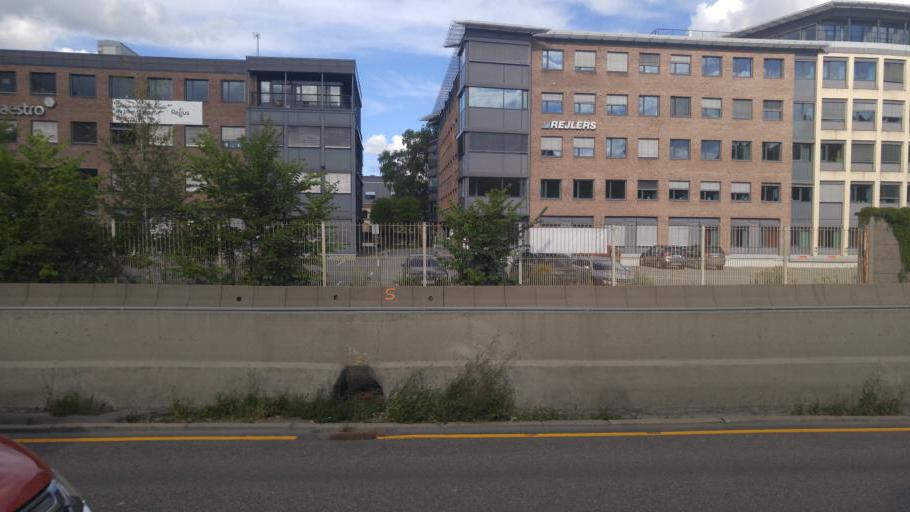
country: NO
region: Oslo
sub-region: Oslo
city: Sjolyststranda
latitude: 59.9183
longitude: 10.6836
